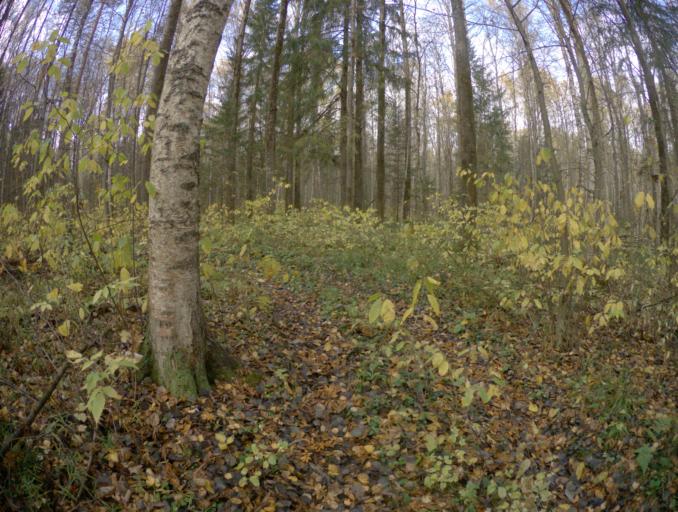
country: RU
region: Vladimir
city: Golovino
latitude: 55.9665
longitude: 40.3746
